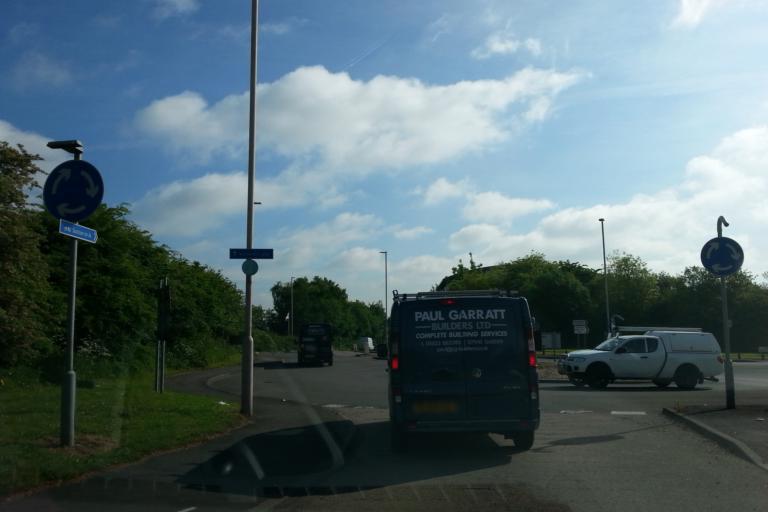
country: GB
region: England
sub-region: Nottinghamshire
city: Mansfield
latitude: 53.1294
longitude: -1.2222
